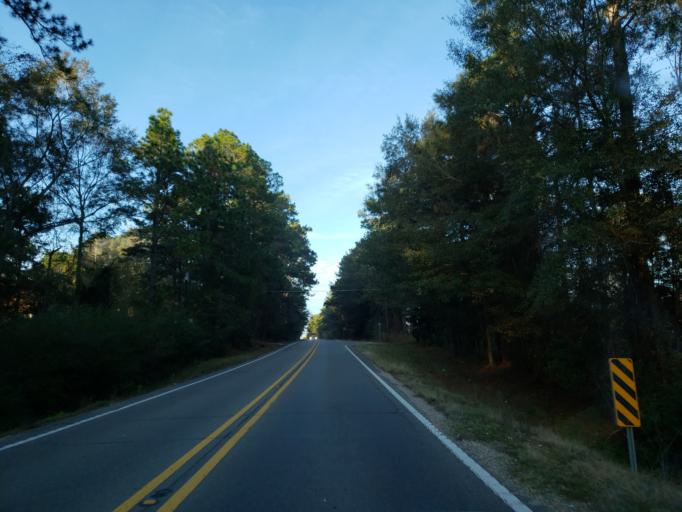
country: US
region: Mississippi
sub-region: Lamar County
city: Purvis
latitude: 31.1533
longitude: -89.3984
